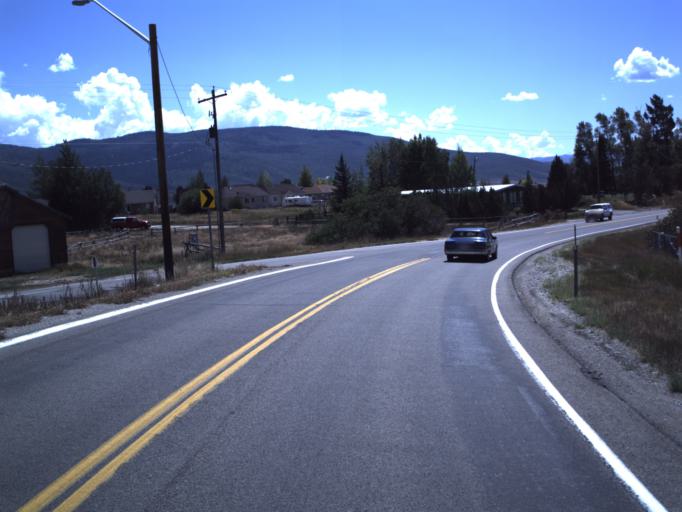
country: US
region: Utah
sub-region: Summit County
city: Oakley
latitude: 40.7232
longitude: -111.3007
